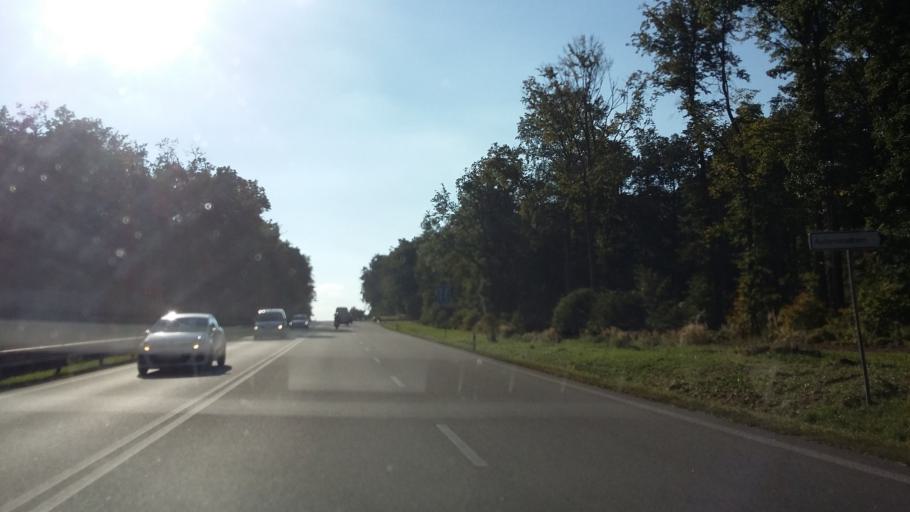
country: CZ
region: South Moravian
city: Troubsko
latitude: 49.1897
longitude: 16.4592
